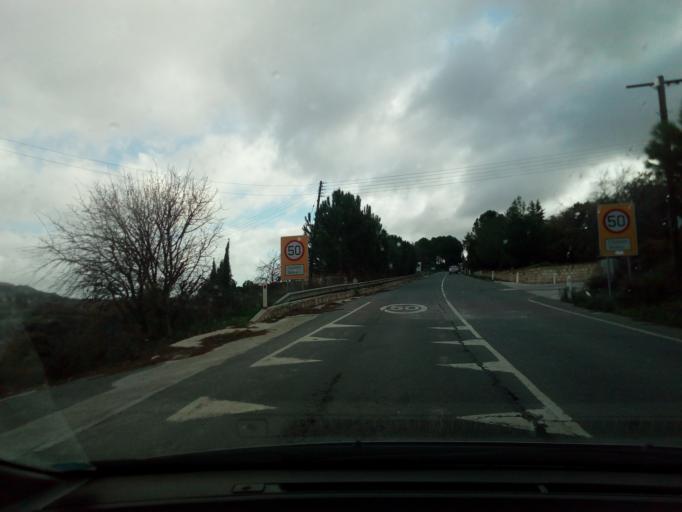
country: CY
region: Pafos
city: Tala
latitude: 34.9265
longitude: 32.4778
